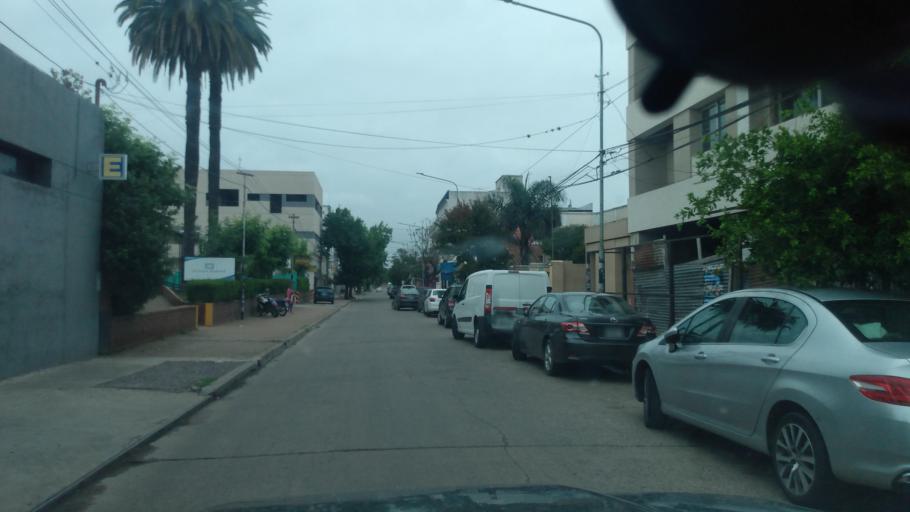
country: AR
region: Buenos Aires
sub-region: Partido de Lujan
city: Lujan
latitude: -34.5696
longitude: -59.1155
